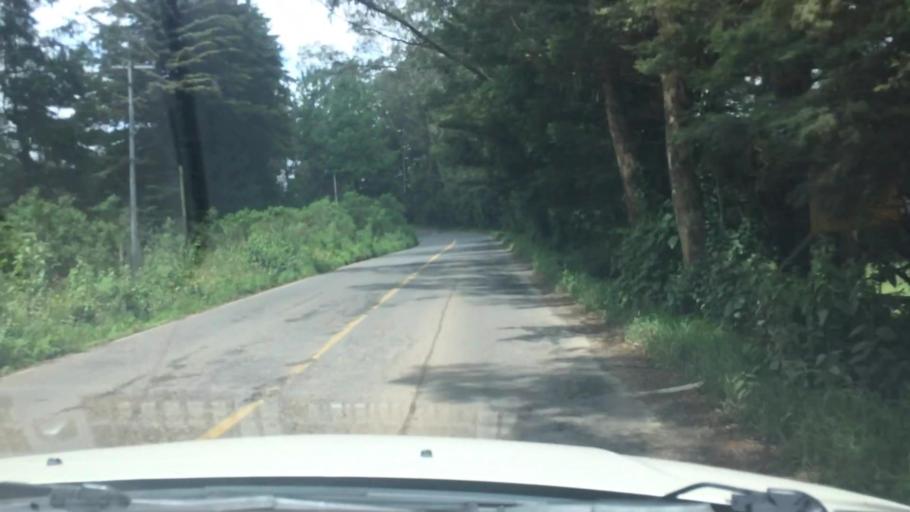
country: MX
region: Mexico
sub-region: Valle de Bravo
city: Cuadrilla de Dolores
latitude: 19.1473
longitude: -100.0649
